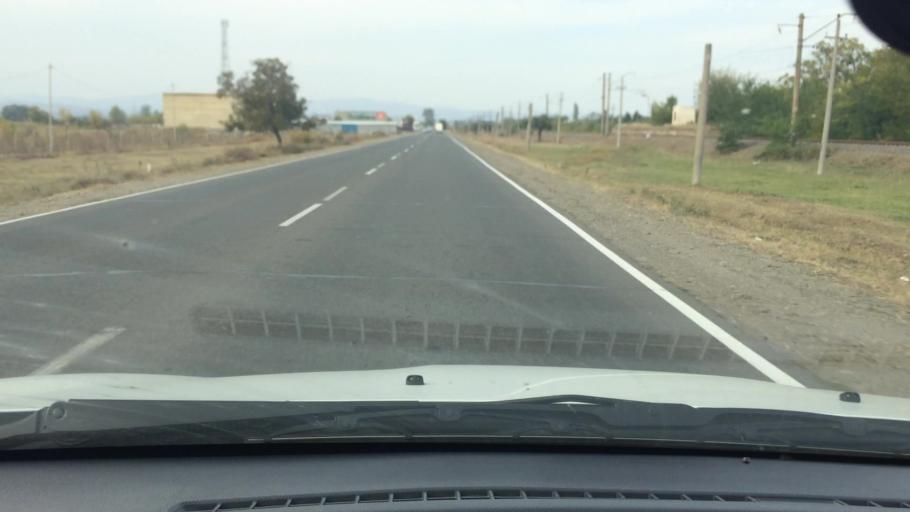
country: GE
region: Kvemo Kartli
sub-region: Marneuli
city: Marneuli
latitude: 41.4336
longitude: 44.8201
